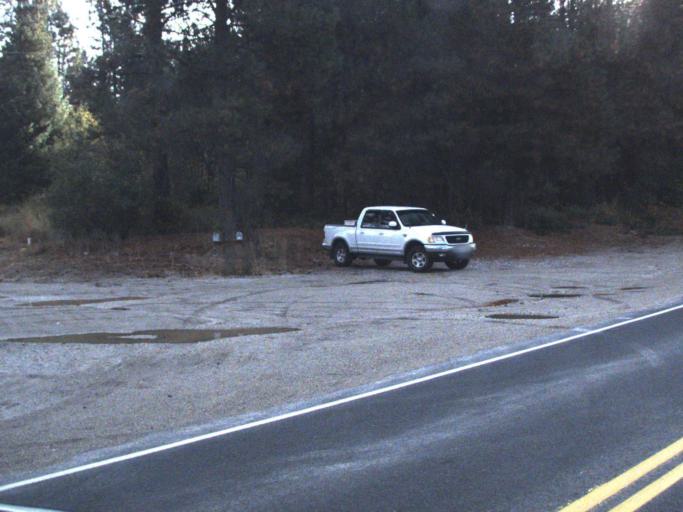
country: US
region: Washington
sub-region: Stevens County
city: Chewelah
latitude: 48.0593
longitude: -117.7557
